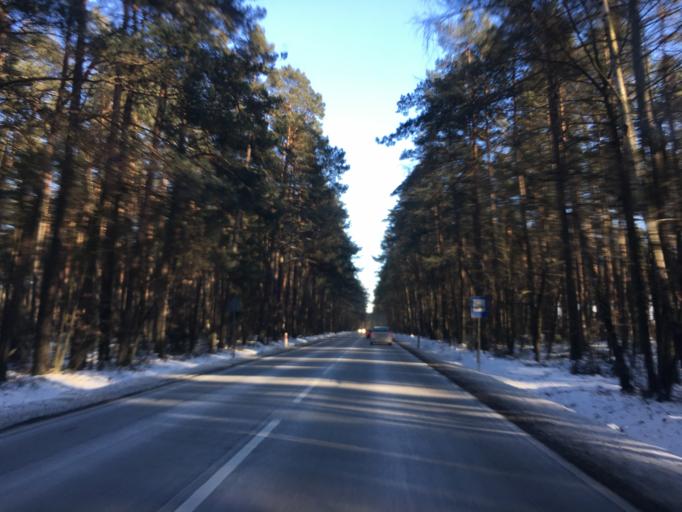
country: PL
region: Pomeranian Voivodeship
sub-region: Powiat koscierski
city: Koscierzyna
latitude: 54.1142
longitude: 17.9038
